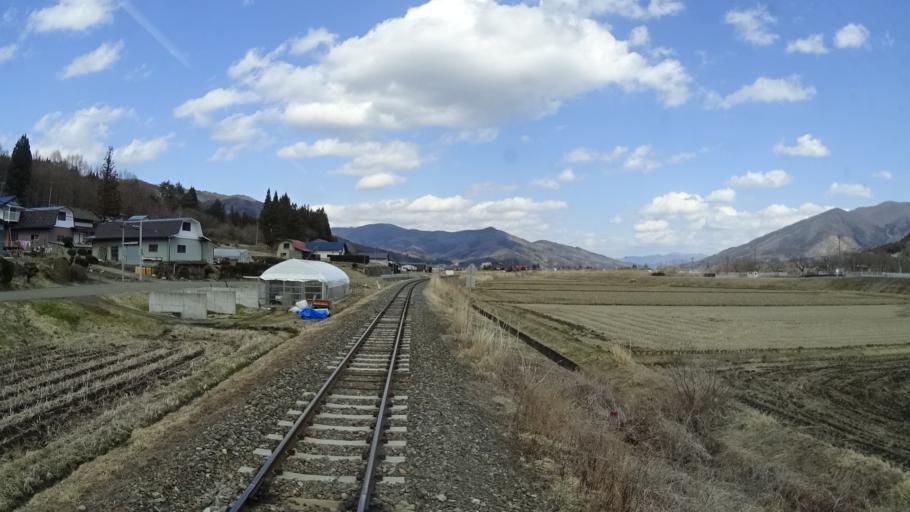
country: JP
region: Iwate
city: Tono
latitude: 39.3183
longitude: 141.4429
